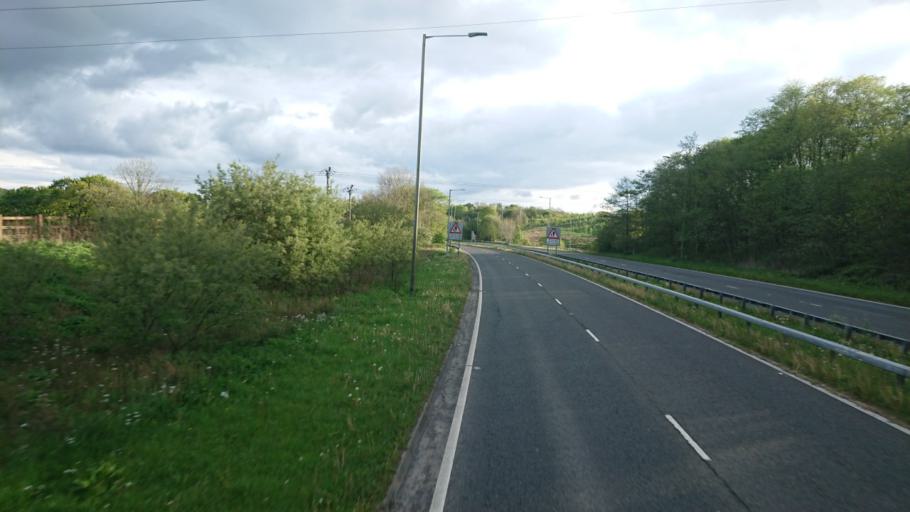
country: GB
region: England
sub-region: Lancashire
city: Rawtenstall
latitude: 53.6959
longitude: -2.3036
